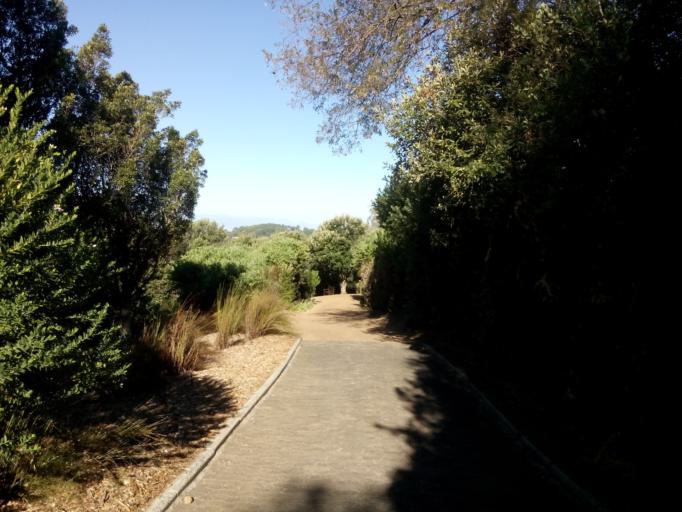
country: ZA
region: Western Cape
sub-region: City of Cape Town
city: Newlands
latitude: -33.9912
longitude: 18.4285
